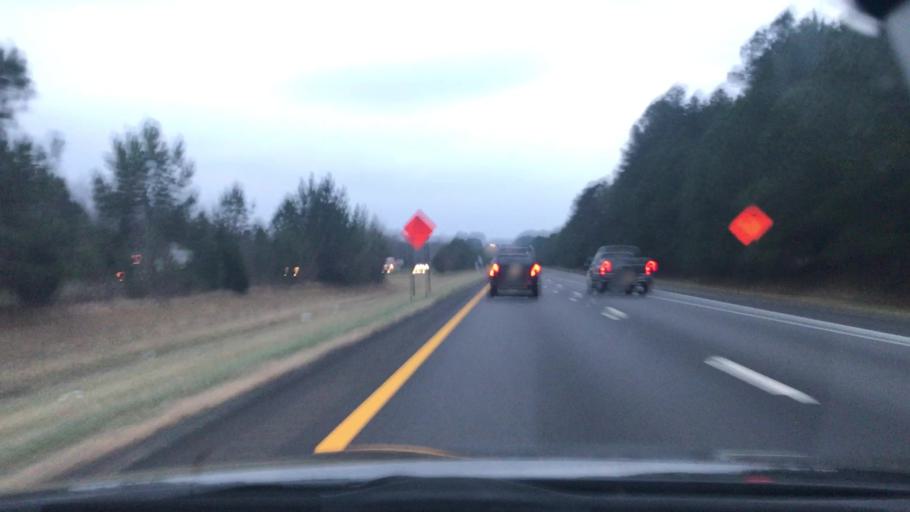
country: US
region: Tennessee
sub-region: Sumner County
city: White House
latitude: 36.4484
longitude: -86.6979
